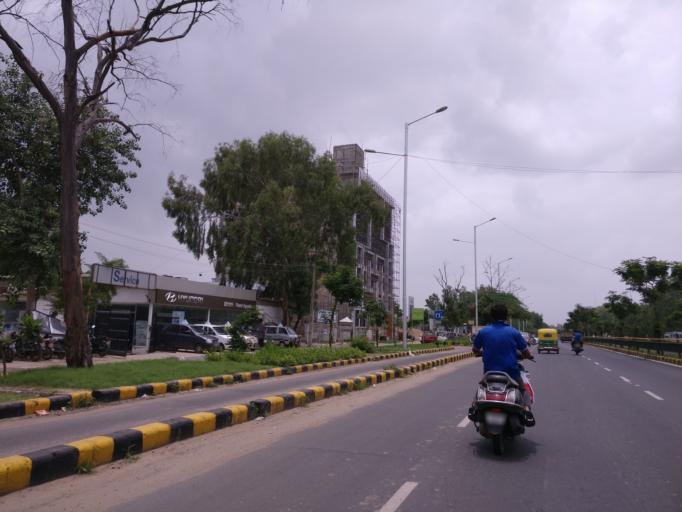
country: IN
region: Gujarat
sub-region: Gandhinagar
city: Adalaj
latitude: 23.1259
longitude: 72.5836
